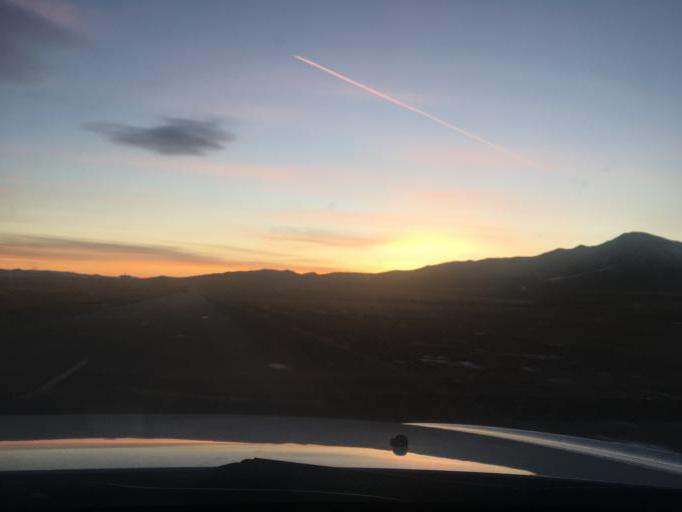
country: MN
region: Central Aimak
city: Mandal
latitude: 48.0896
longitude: 106.6003
